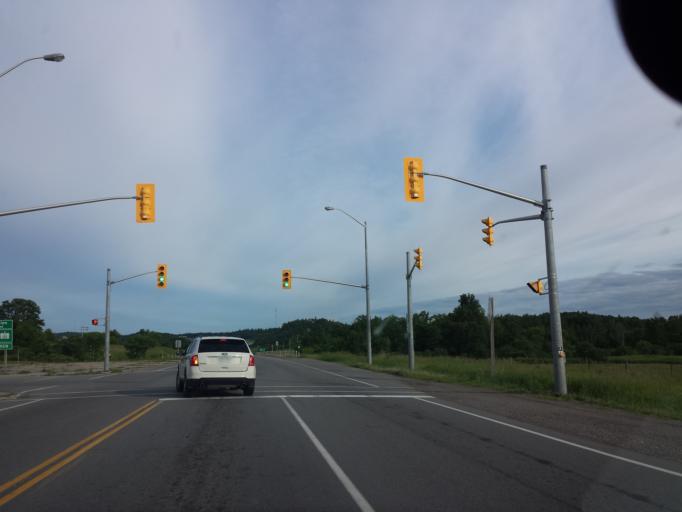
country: CA
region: Ontario
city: Renfrew
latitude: 45.4824
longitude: -76.6457
